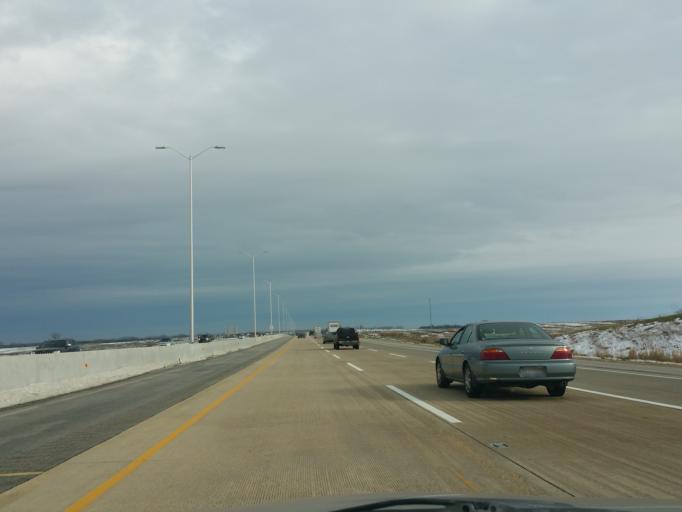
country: US
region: Illinois
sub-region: Boone County
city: Belvidere
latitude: 42.2337
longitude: -88.7986
